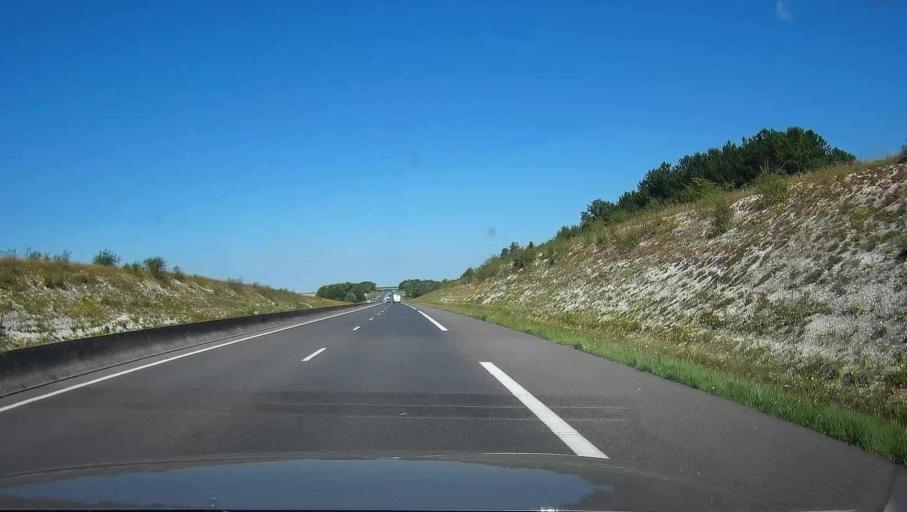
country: FR
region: Champagne-Ardenne
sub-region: Departement de la Marne
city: Compertrix
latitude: 48.8200
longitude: 4.2899
